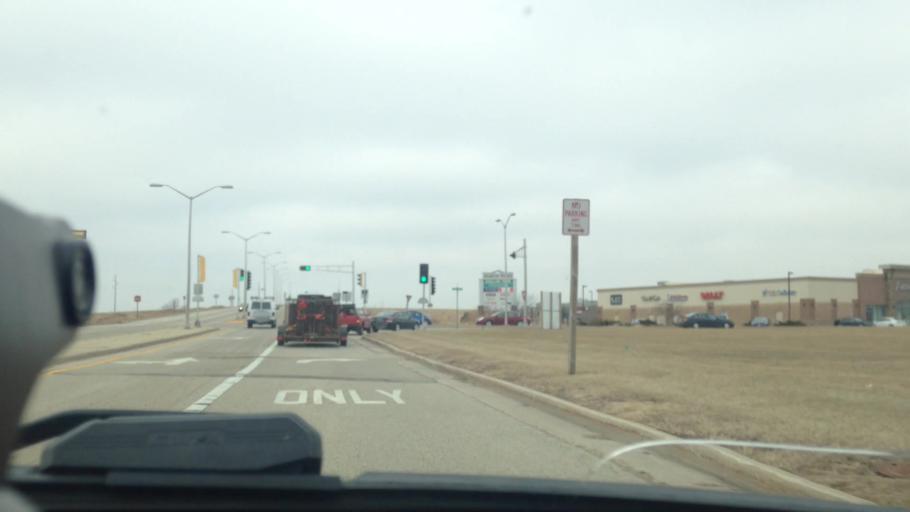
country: US
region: Wisconsin
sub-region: Dodge County
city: Beaver Dam
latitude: 43.4853
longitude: -88.8094
